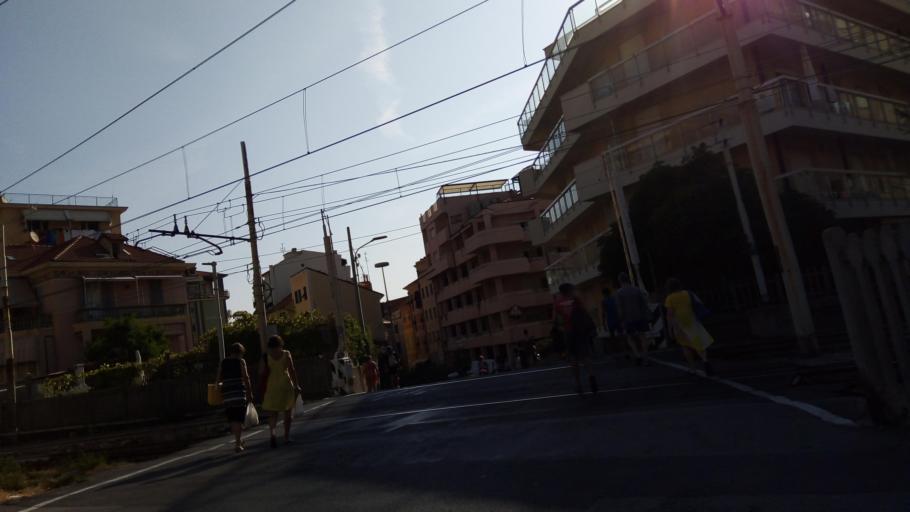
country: IT
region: Liguria
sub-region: Provincia di Savona
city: Loano
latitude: 44.1239
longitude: 8.2552
